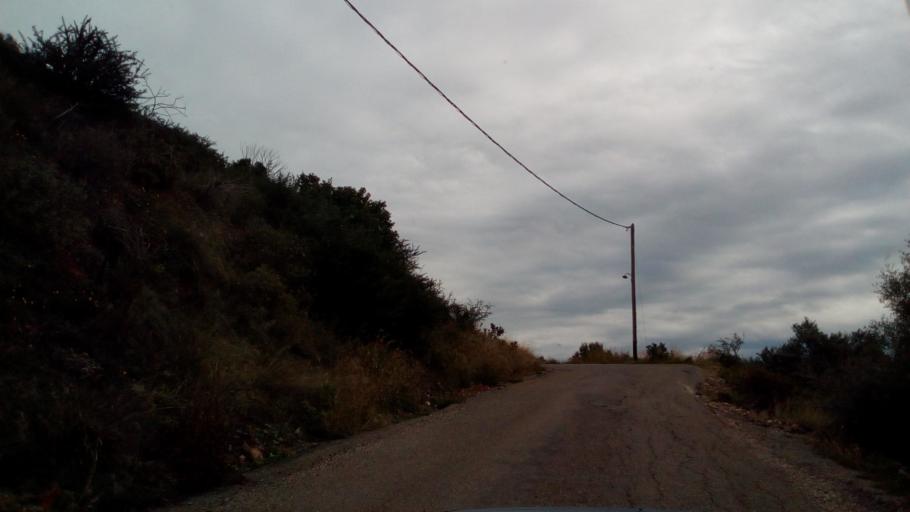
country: GR
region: West Greece
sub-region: Nomos Achaias
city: Kamarai
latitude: 38.4076
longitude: 21.9523
